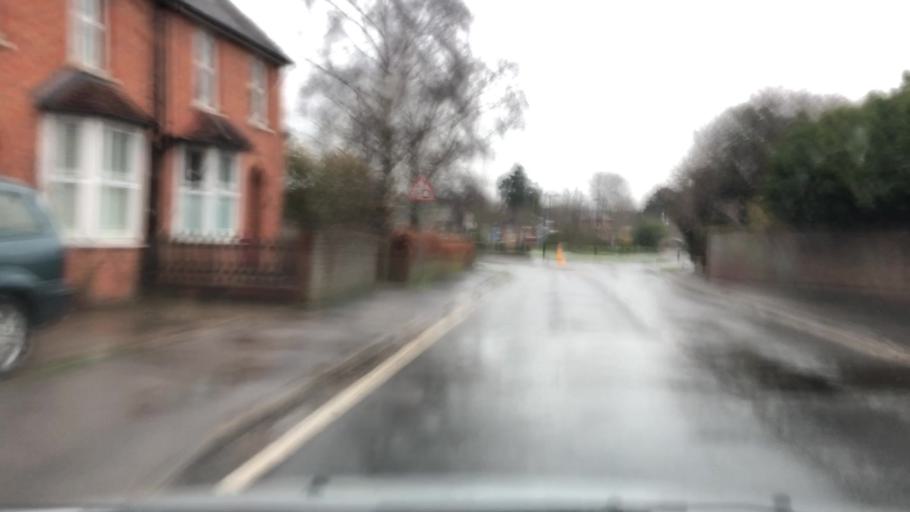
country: GB
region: England
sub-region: Hampshire
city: Odiham
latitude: 51.2589
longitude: -0.9527
